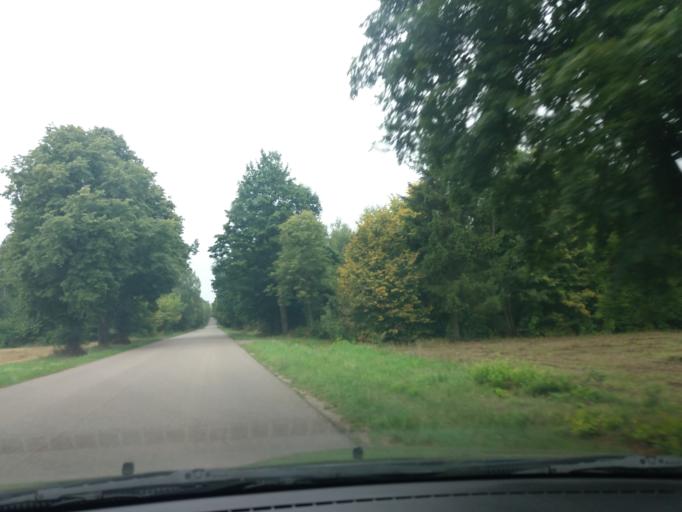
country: PL
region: Masovian Voivodeship
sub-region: Powiat mlawski
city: Wieczfnia Koscielna
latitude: 53.2132
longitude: 20.5062
